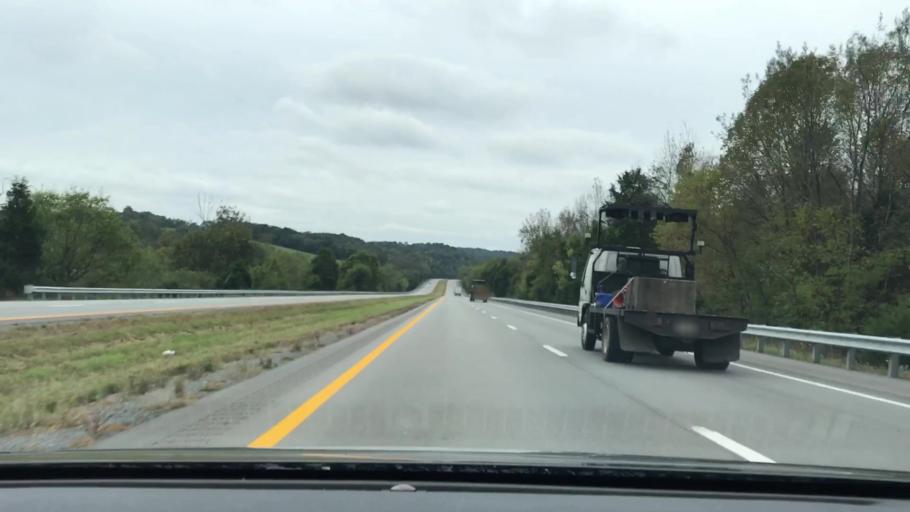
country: US
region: Kentucky
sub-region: Adair County
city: Columbia
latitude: 37.0674
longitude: -85.4158
